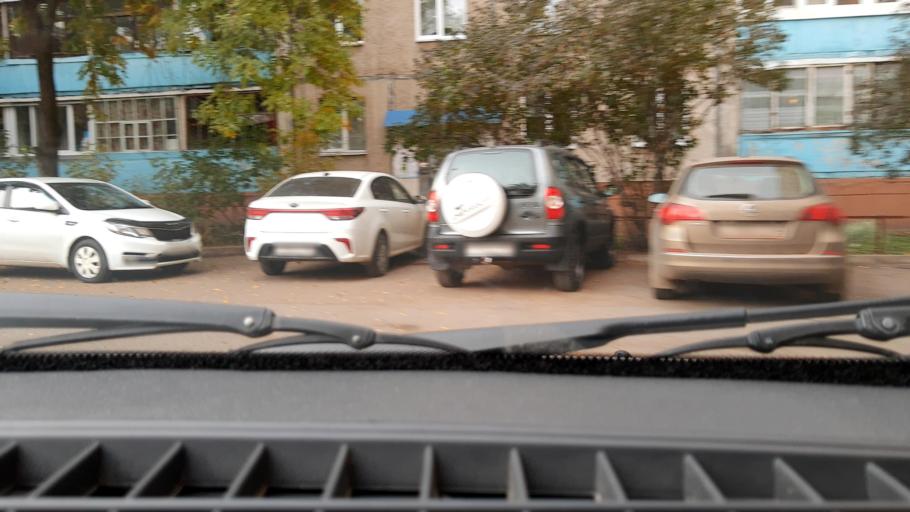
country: RU
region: Bashkortostan
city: Ufa
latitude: 54.8139
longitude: 56.1340
